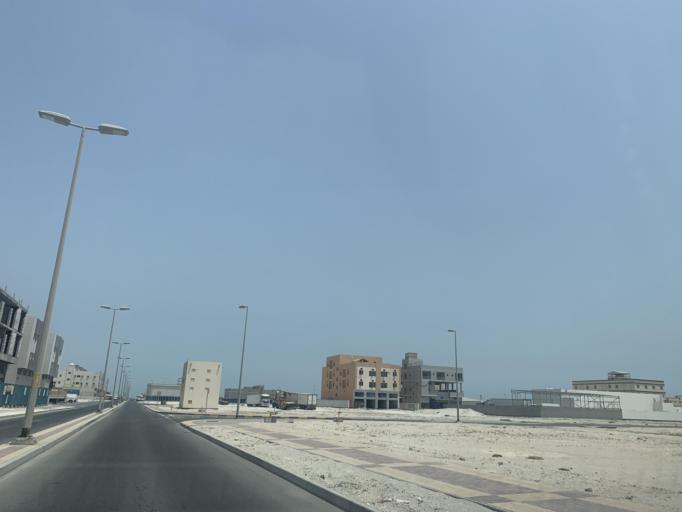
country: BH
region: Muharraq
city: Al Hadd
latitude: 26.2599
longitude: 50.6667
